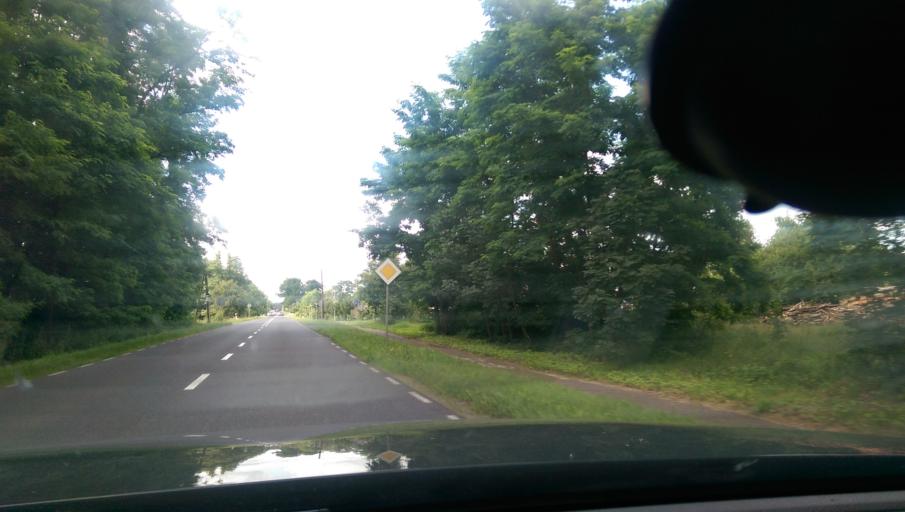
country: PL
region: Lubusz
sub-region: Powiat slubicki
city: Osno Lubuskie
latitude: 52.4937
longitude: 14.9111
